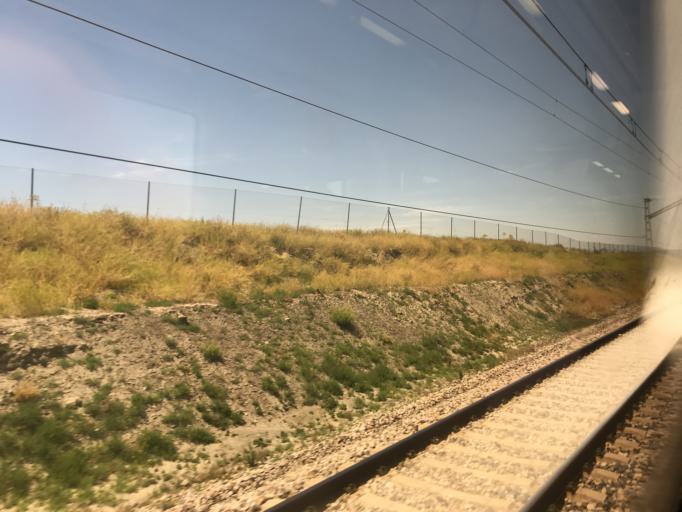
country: ES
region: Madrid
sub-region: Provincia de Madrid
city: Getafe
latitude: 40.2845
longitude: -3.7043
